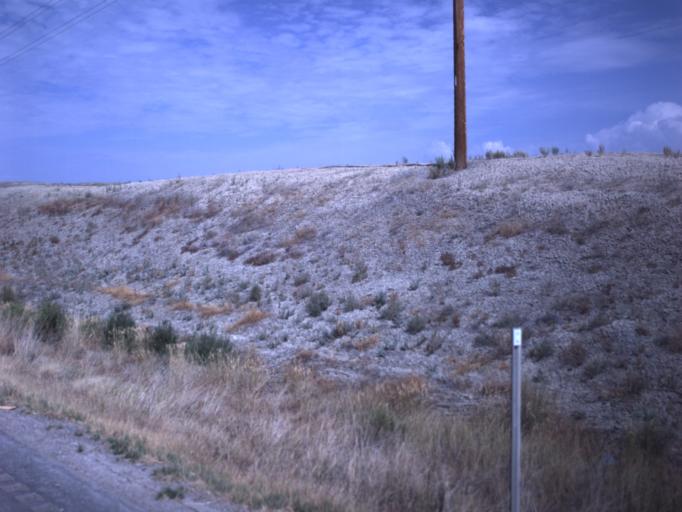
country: US
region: Utah
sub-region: Uintah County
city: Naples
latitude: 40.3693
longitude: -109.3875
